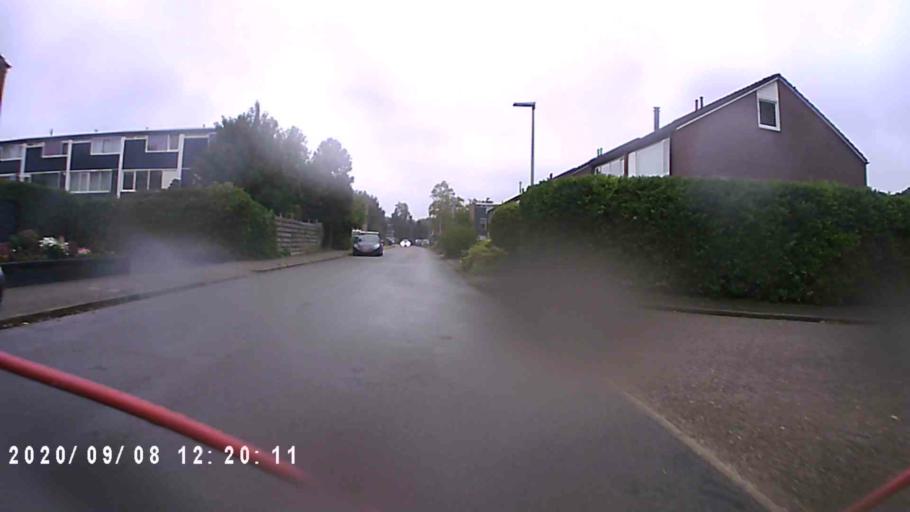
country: NL
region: Groningen
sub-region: Gemeente Veendam
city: Veendam
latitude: 53.0917
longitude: 6.8492
